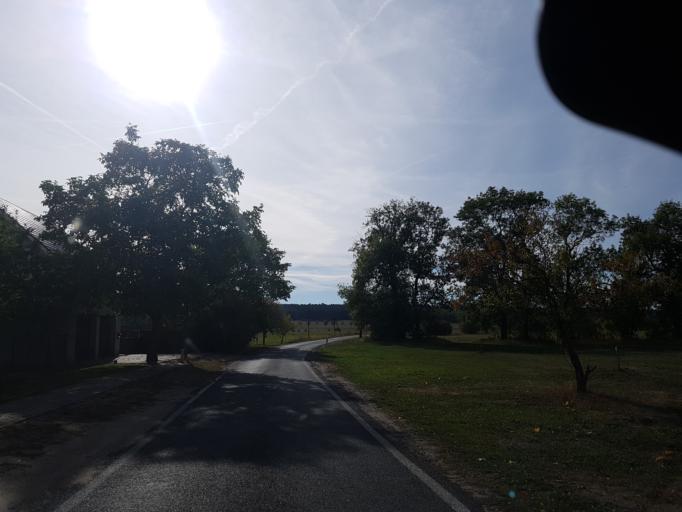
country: DE
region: Brandenburg
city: Ihlow
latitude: 51.8193
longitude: 13.2828
